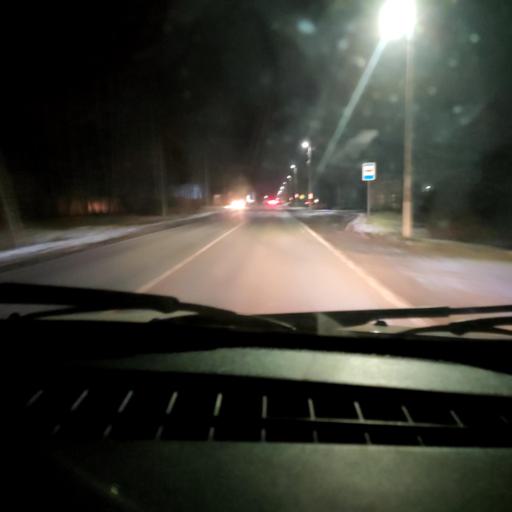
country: RU
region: Voronezj
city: Podgornoye
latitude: 51.7879
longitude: 39.1657
